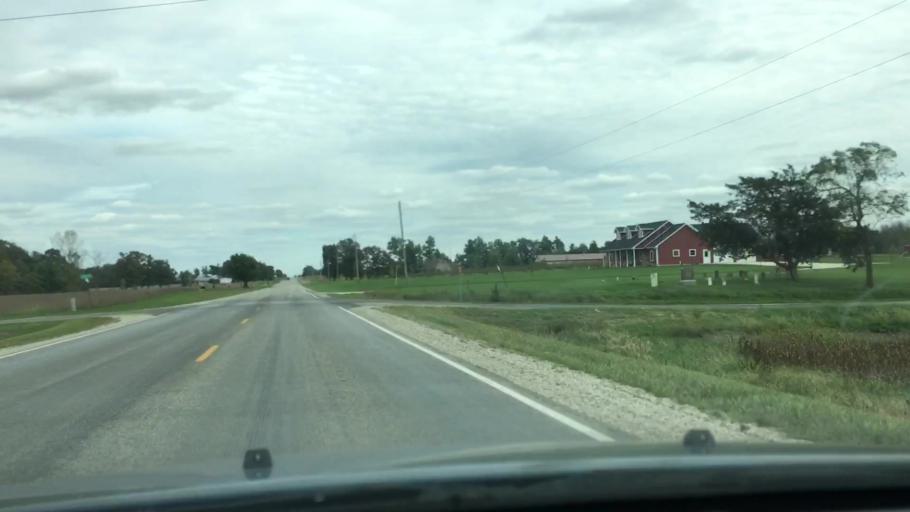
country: US
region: Indiana
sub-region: Adams County
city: Geneva
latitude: 40.5416
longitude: -84.9154
